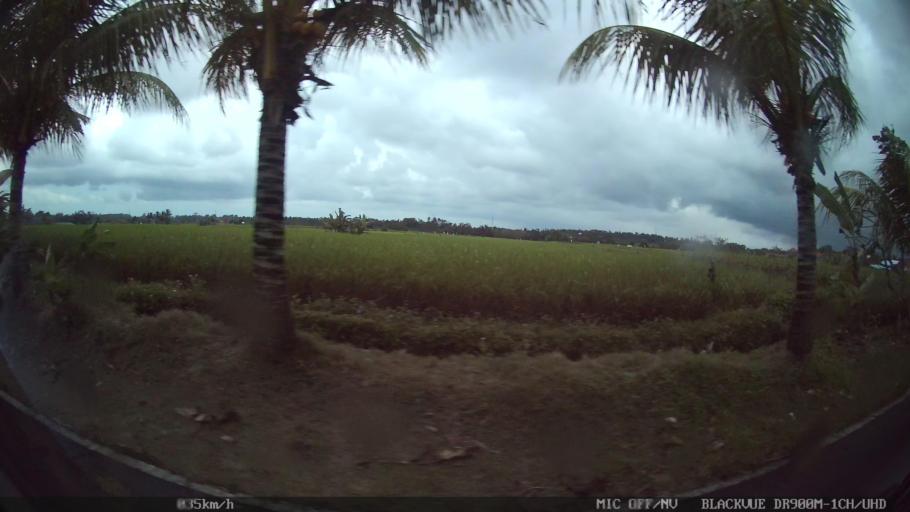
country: ID
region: Bali
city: Banjar Cemenggon
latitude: -8.5309
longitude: 115.1892
